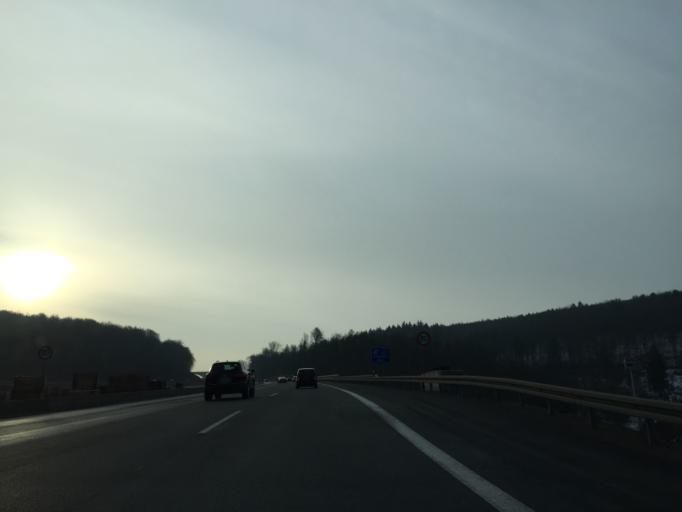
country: DE
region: Bavaria
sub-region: Regierungsbezirk Unterfranken
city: Weibersbrunn
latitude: 49.9464
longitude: 9.3350
